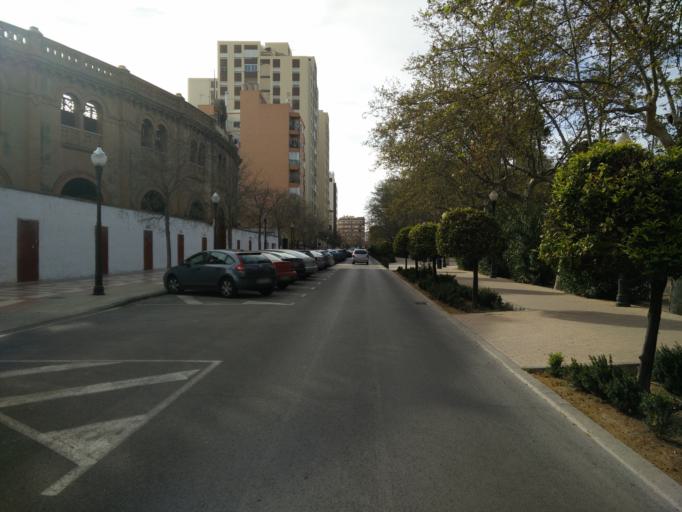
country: ES
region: Valencia
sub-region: Provincia de Castello
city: Castello de la Plana
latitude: 39.9862
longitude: -0.0447
